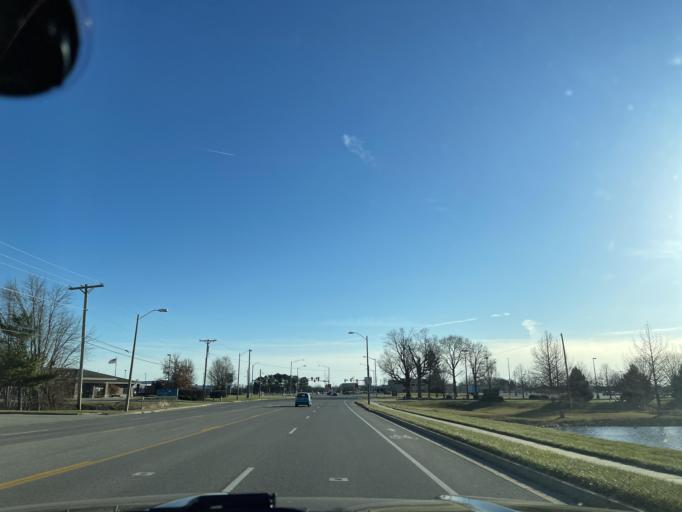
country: US
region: Illinois
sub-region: Sangamon County
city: Jerome
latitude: 39.7622
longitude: -89.7154
